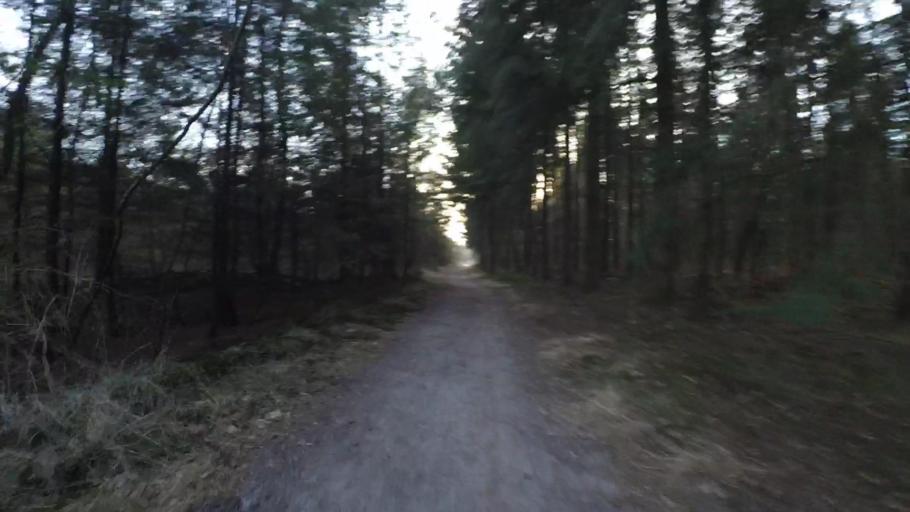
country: NL
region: Utrecht
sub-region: Gemeente Utrechtse Heuvelrug
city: Maarn
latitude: 52.0911
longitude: 5.3561
